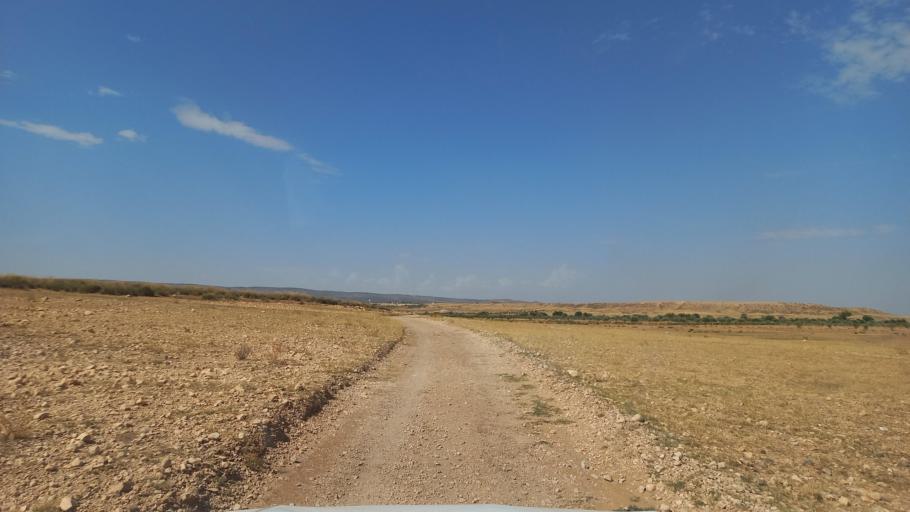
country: TN
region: Al Qasrayn
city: Kasserine
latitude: 35.2542
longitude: 8.9564
